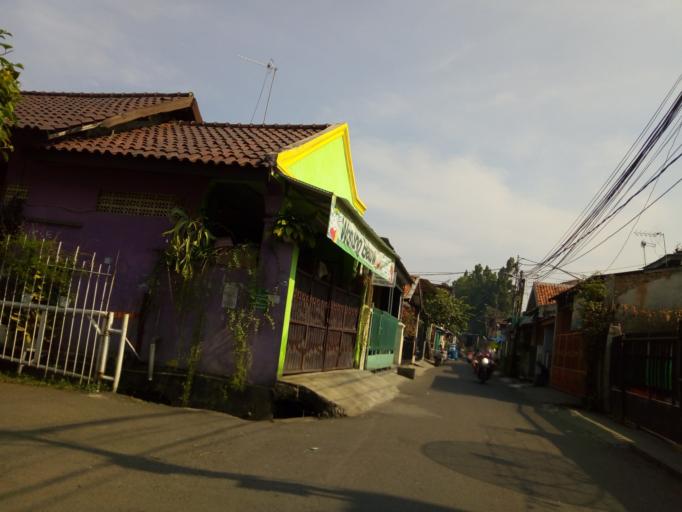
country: ID
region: Jakarta Raya
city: Jakarta
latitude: -6.2098
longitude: 106.8390
